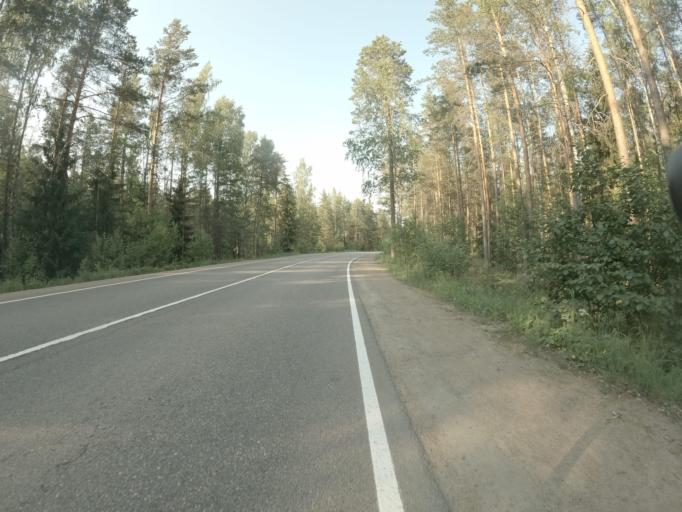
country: RU
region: Leningrad
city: Veshchevo
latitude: 60.4669
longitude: 29.2463
